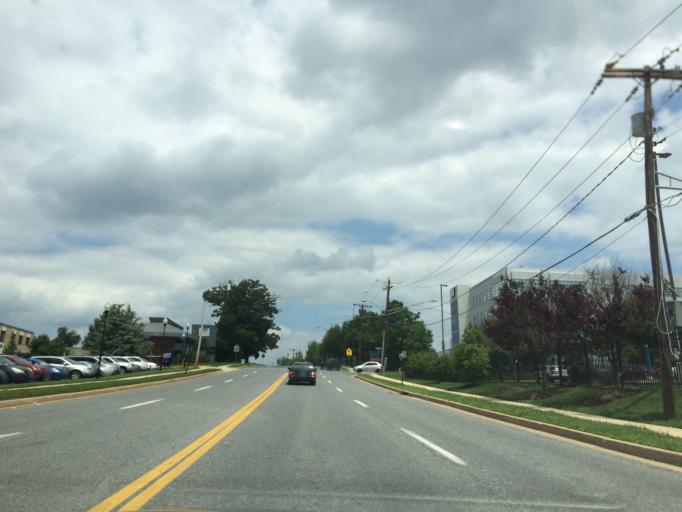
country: US
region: Maryland
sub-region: Baltimore County
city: Randallstown
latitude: 39.3588
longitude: -76.7842
